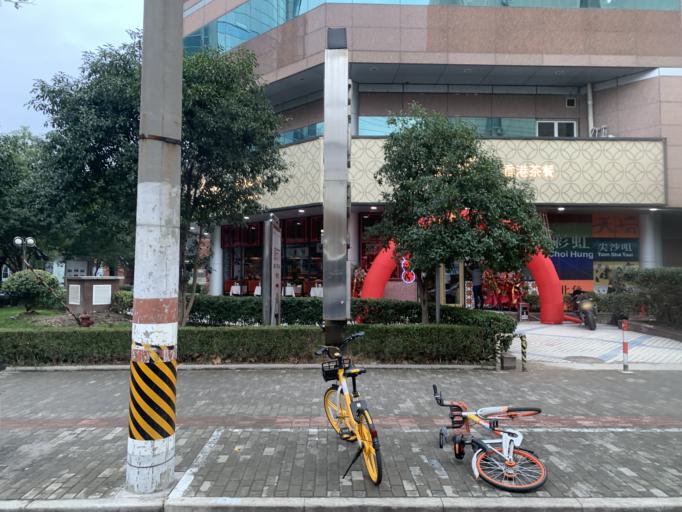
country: CN
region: Shanghai Shi
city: Pudong
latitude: 31.2289
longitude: 121.5191
